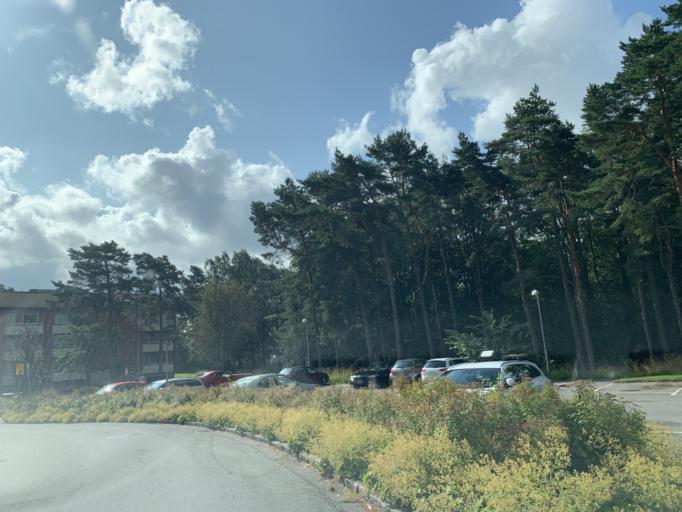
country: SE
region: Vaestra Goetaland
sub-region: Goteborg
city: Eriksbo
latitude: 57.7501
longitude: 12.0327
